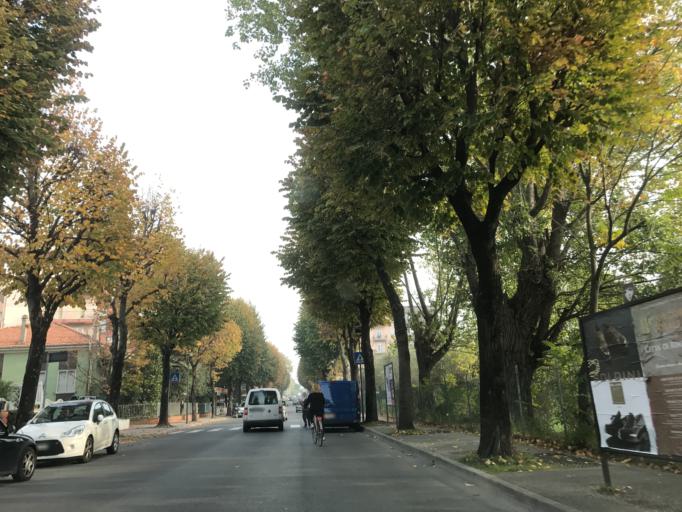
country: IT
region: Emilia-Romagna
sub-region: Provincia di Rimini
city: Rimini
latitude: 44.0752
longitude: 12.5575
